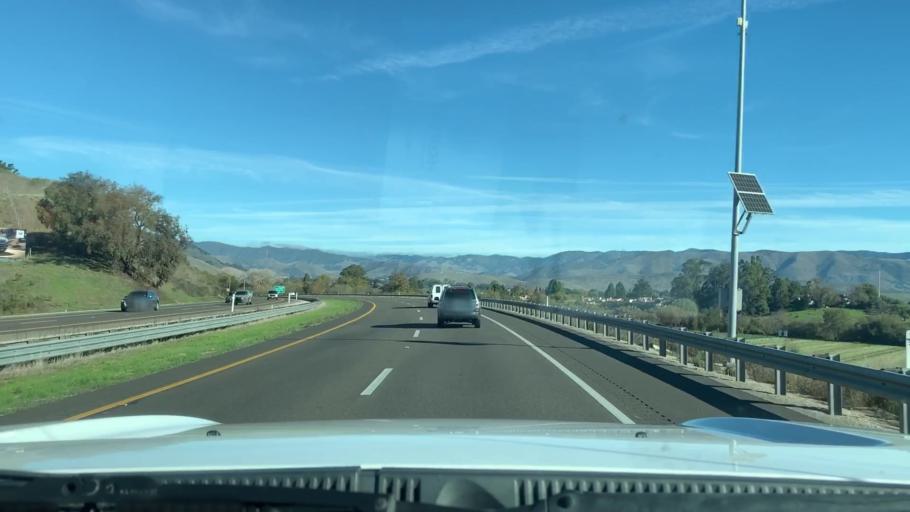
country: US
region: California
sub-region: San Luis Obispo County
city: San Luis Obispo
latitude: 35.2363
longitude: -120.6841
